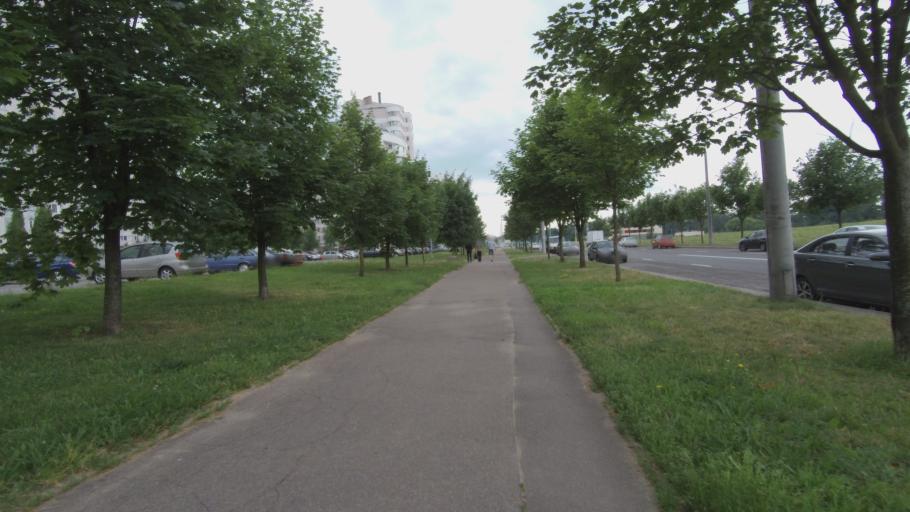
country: BY
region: Minsk
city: Syenitsa
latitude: 53.8481
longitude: 27.5593
